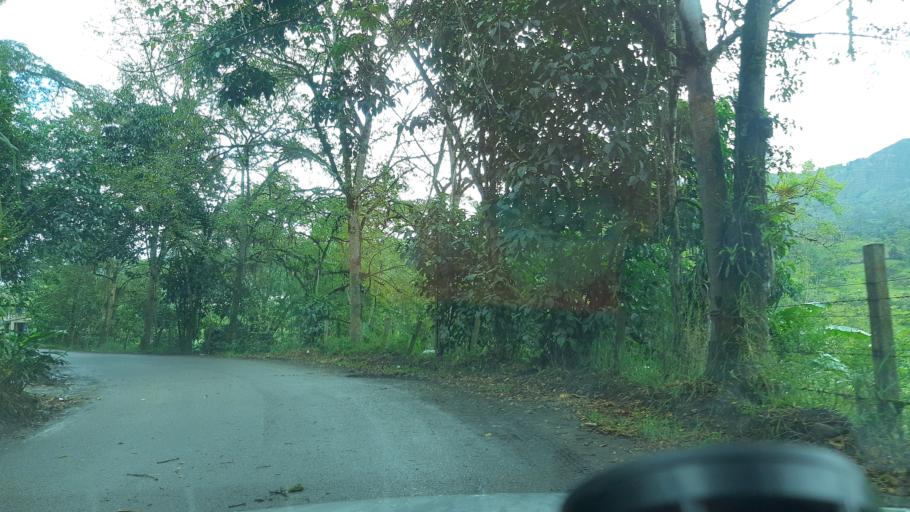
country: CO
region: Boyaca
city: Chinavita
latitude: 5.1338
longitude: -73.3627
